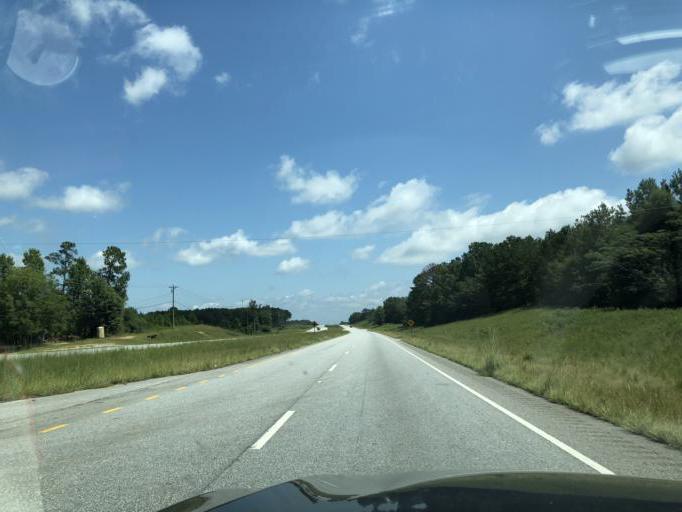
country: US
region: Alabama
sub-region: Barbour County
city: Eufaula
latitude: 31.7562
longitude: -85.2137
